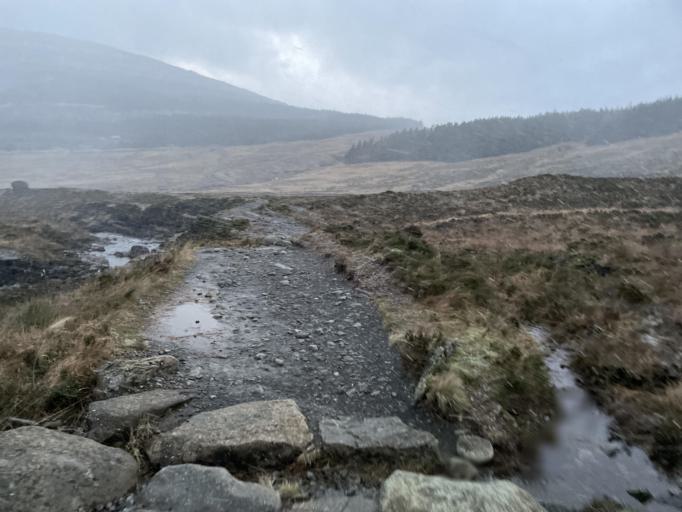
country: GB
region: Scotland
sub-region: Highland
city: Isle of Skye
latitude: 57.2498
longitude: -6.2630
